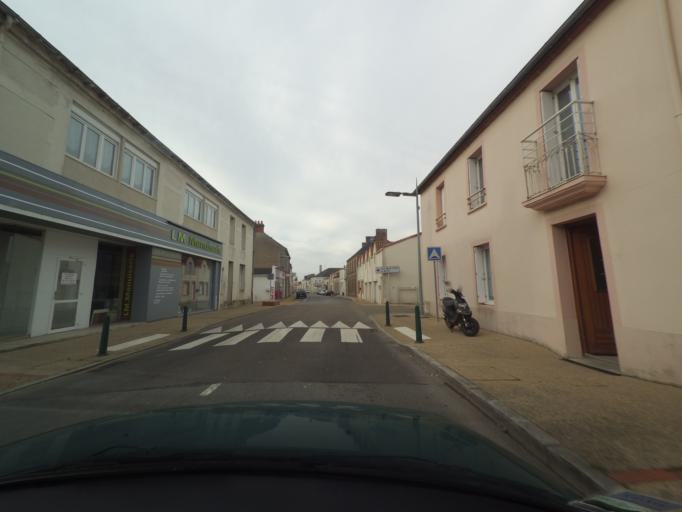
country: FR
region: Pays de la Loire
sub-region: Departement de la Loire-Atlantique
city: Arthon-en-Retz
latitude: 47.1155
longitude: -1.9405
